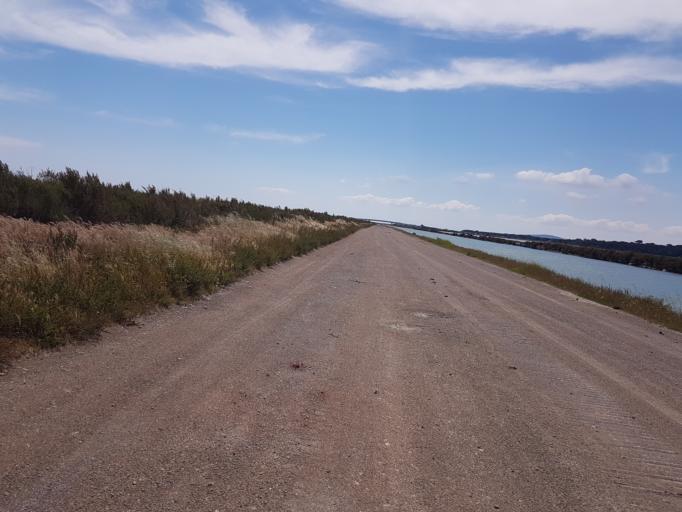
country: FR
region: Languedoc-Roussillon
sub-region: Departement de l'Herault
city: Vic-la-Gardiole
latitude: 43.4726
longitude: 3.8266
